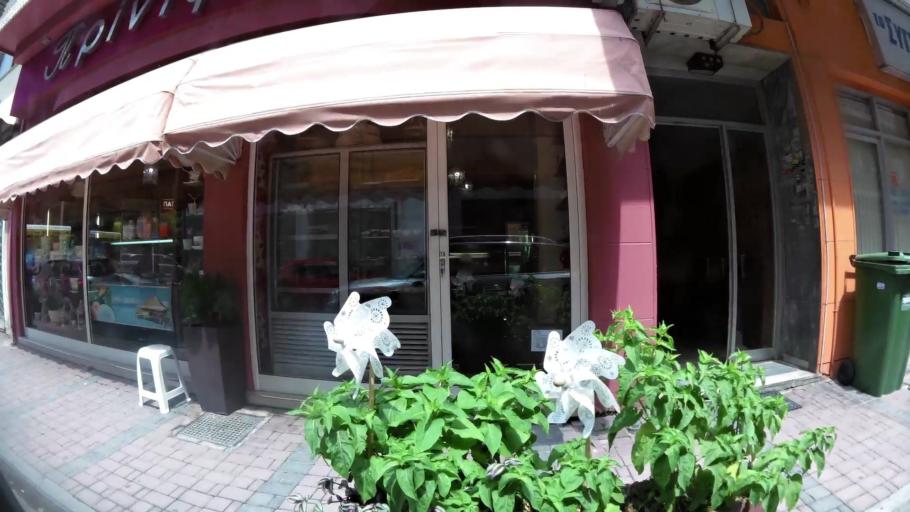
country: GR
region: Central Macedonia
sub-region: Nomos Pierias
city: Katerini
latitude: 40.2693
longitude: 22.5110
